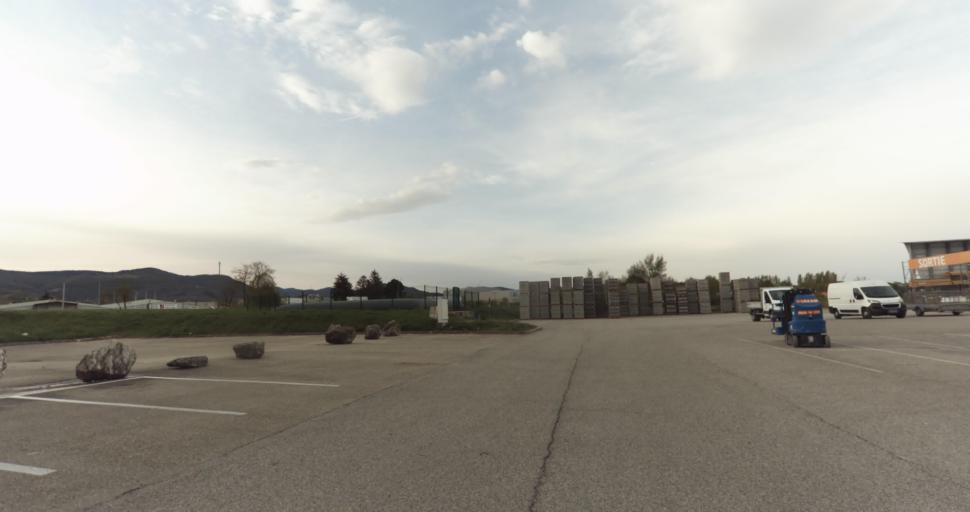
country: FR
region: Rhone-Alpes
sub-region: Departement de l'Ain
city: Amberieu-en-Bugey
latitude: 45.9711
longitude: 5.3397
